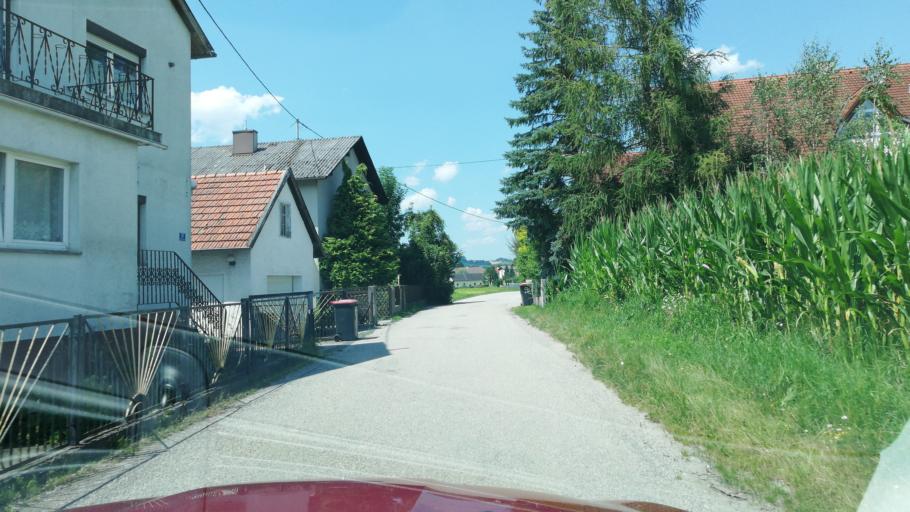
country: AT
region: Upper Austria
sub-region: Wels-Land
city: Buchkirchen
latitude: 48.2169
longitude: 13.9755
